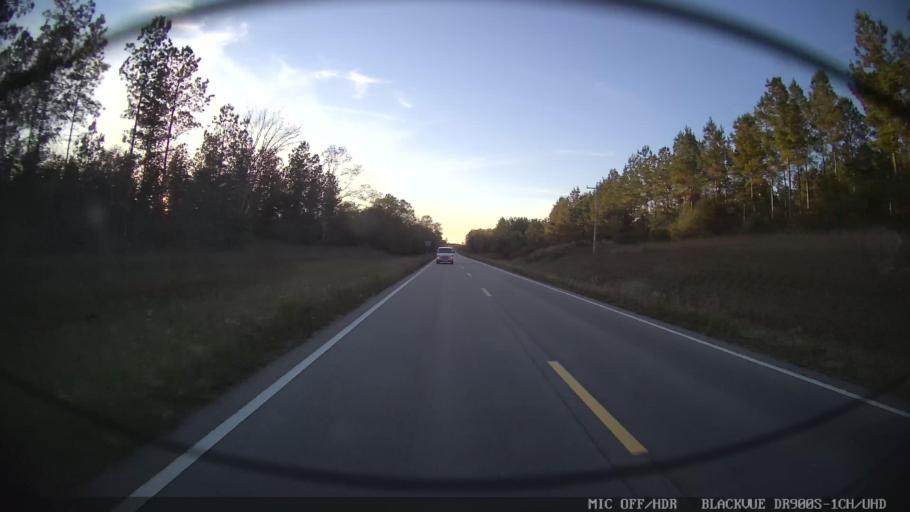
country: US
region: Mississippi
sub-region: Lamar County
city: Lumberton
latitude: 30.9907
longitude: -89.2720
